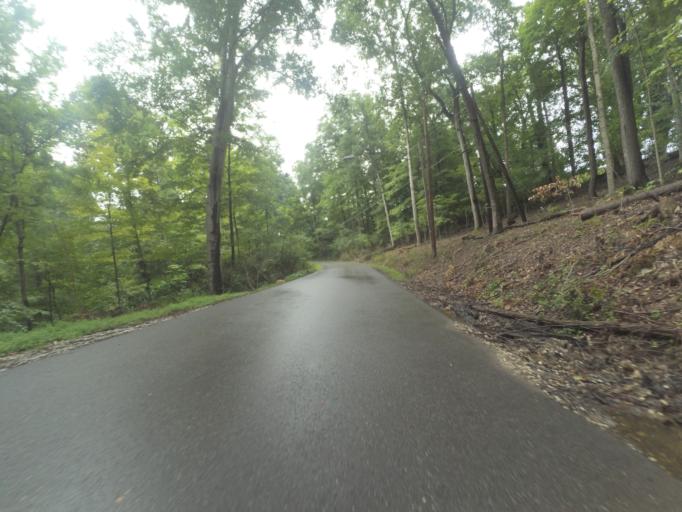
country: US
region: West Virginia
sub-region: Cabell County
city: Huntington
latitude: 38.4022
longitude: -82.4519
